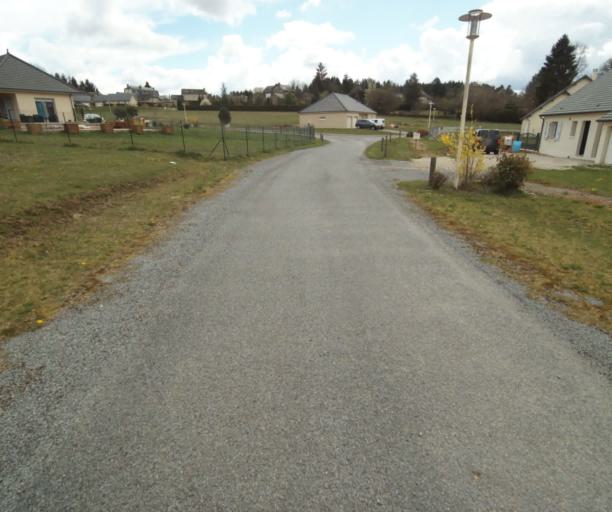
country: FR
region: Limousin
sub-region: Departement de la Correze
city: Correze
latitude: 45.3370
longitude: 1.9435
